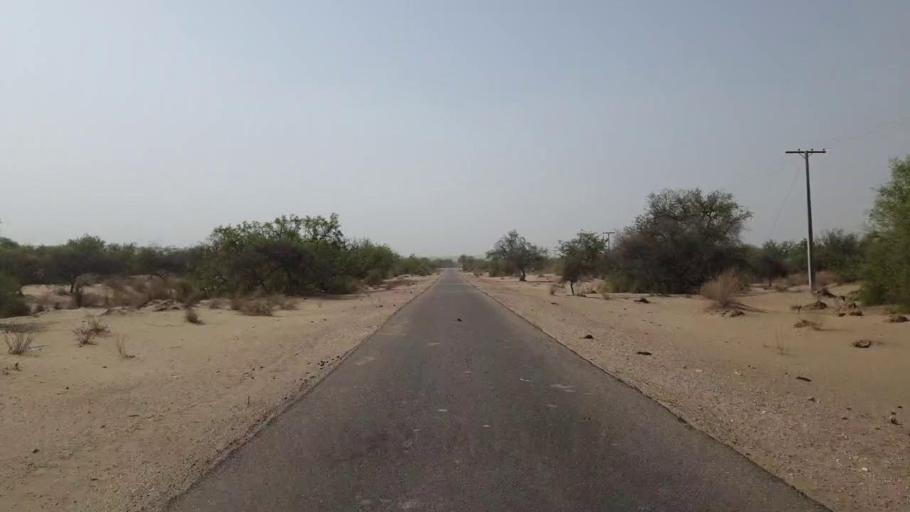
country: PK
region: Sindh
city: Mithi
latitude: 24.6017
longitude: 69.9233
